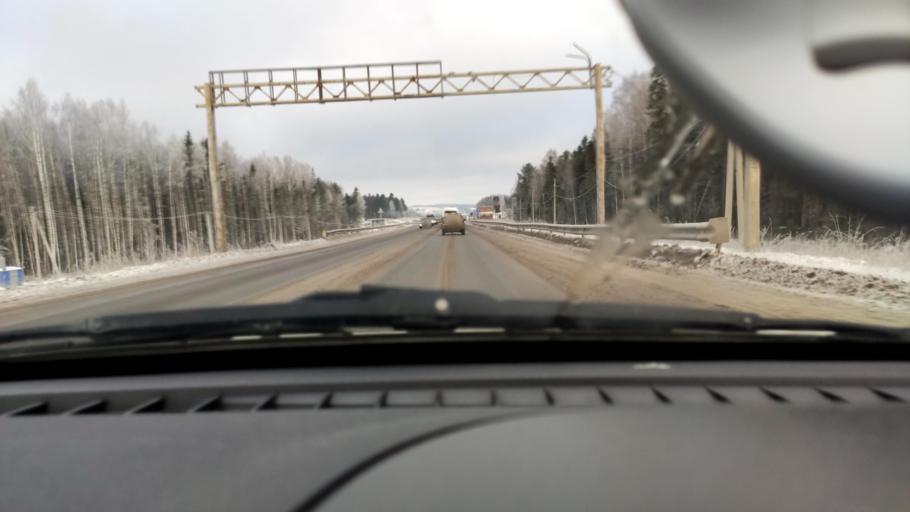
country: RU
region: Perm
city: Polazna
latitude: 58.1454
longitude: 56.4196
